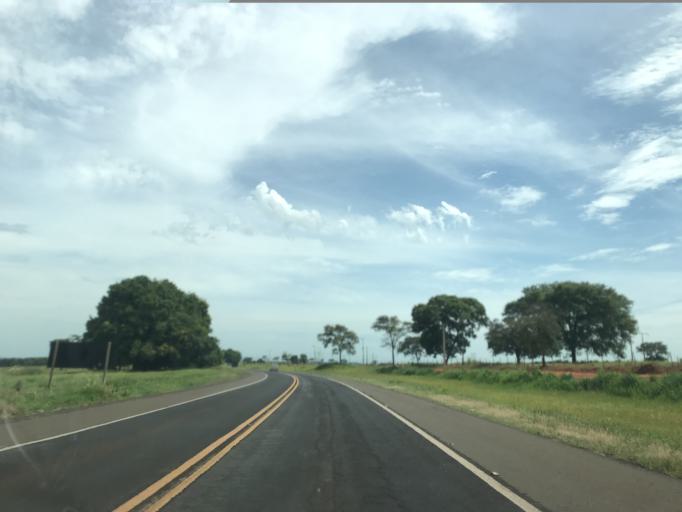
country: BR
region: Sao Paulo
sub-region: Nova Granada
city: Nova Granada
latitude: -20.3534
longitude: -49.2149
